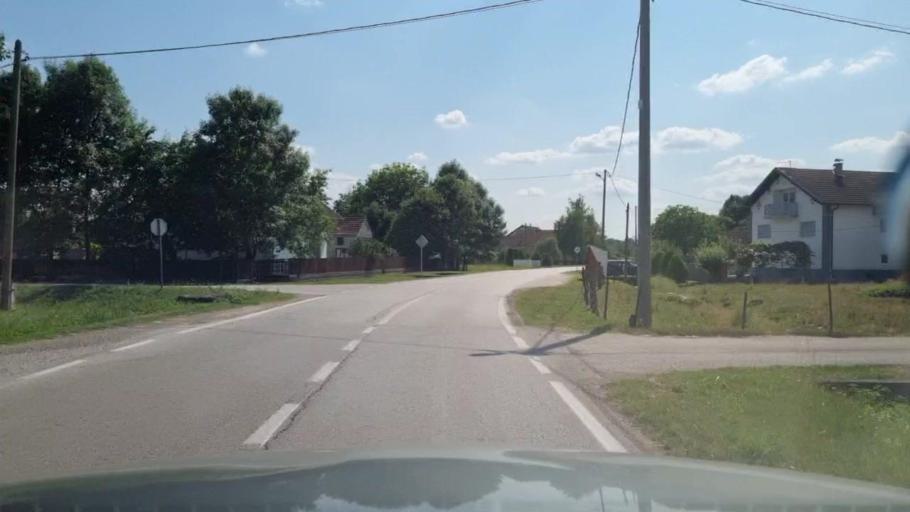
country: BA
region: Federation of Bosnia and Herzegovina
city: Donja Dubica
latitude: 45.0560
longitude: 18.3861
